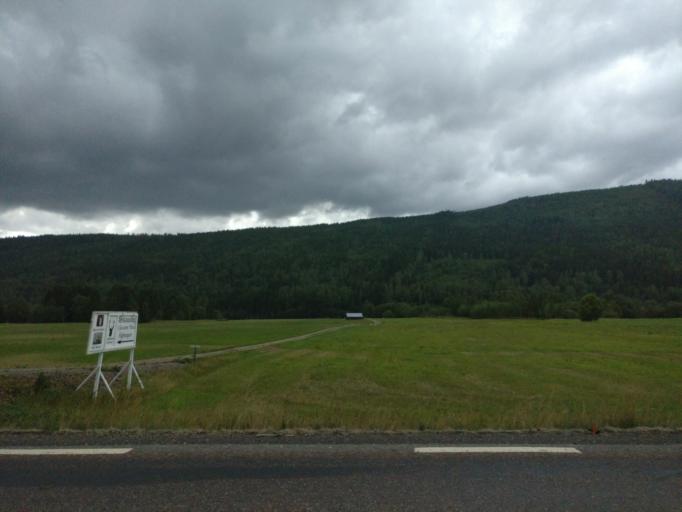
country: SE
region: Vaermland
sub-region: Torsby Kommun
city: Torsby
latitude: 60.7051
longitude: 12.8974
